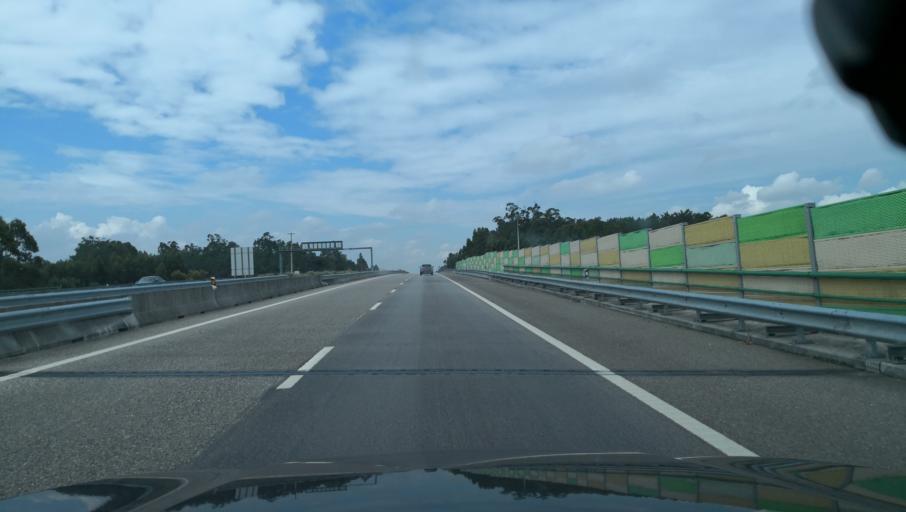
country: PT
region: Leiria
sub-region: Leiria
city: Amor
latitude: 39.7968
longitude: -8.8555
